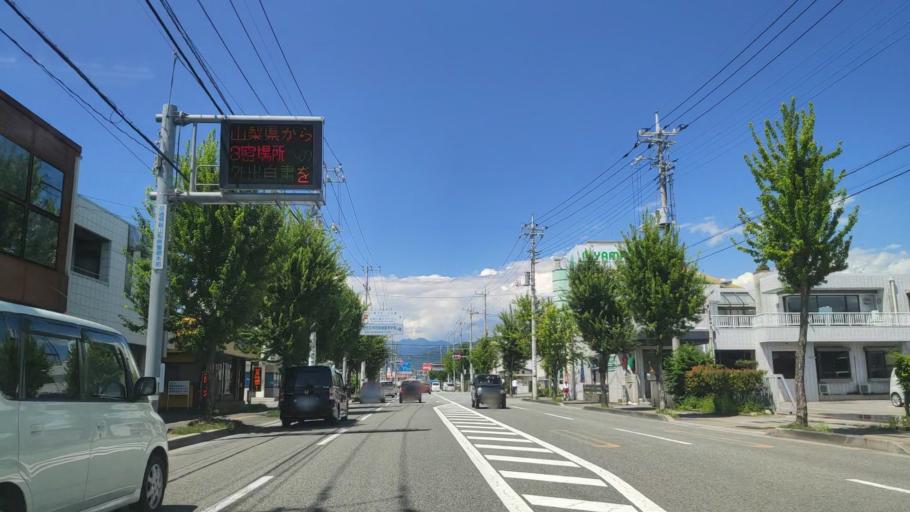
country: JP
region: Yamanashi
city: Kofu-shi
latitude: 35.6272
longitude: 138.5717
